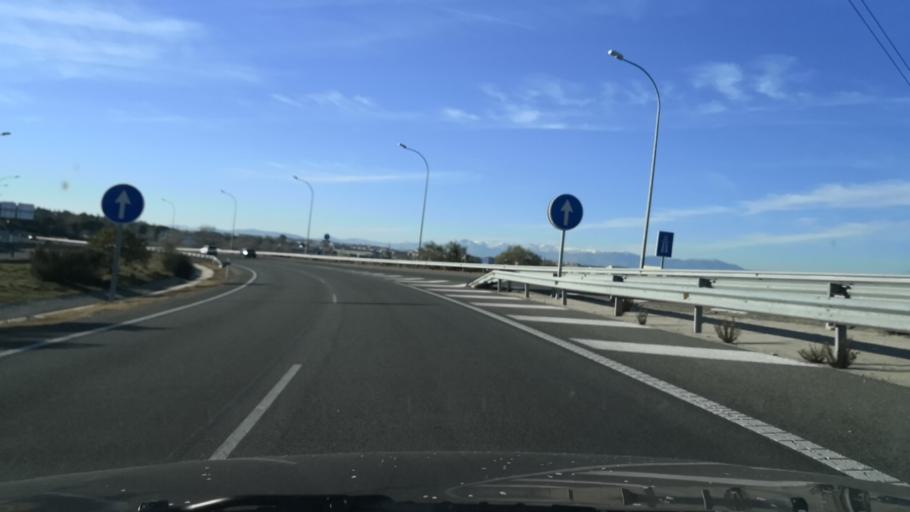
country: ES
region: Madrid
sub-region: Provincia de Madrid
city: San Sebastian de los Reyes
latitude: 40.5270
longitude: -3.6001
